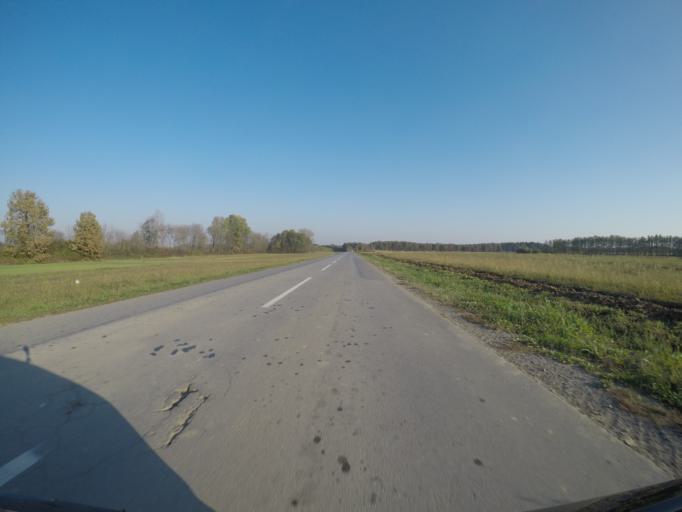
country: HR
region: Virovitick-Podravska
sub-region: Grad Virovitica
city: Virovitica
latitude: 45.8828
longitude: 17.3898
